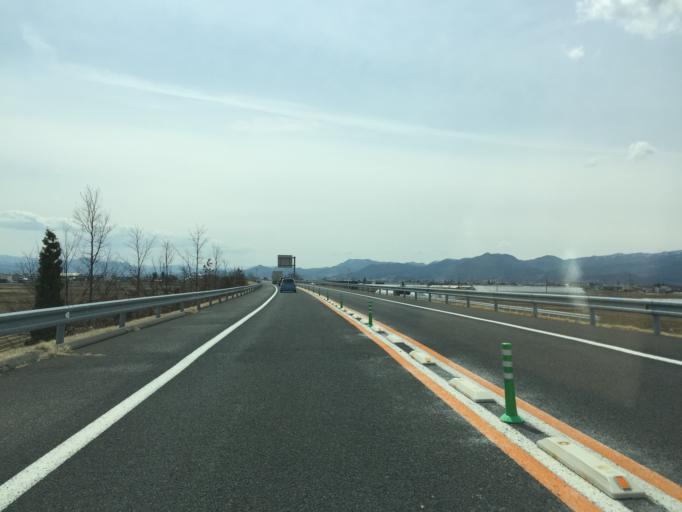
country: JP
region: Yamagata
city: Yamagata-shi
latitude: 38.2923
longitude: 140.2998
